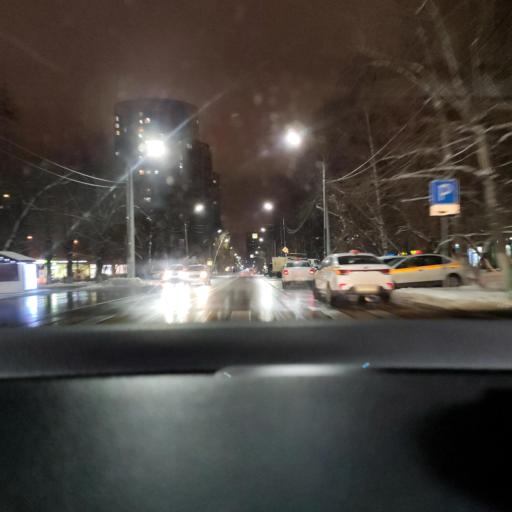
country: RU
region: Moskovskaya
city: Reutov
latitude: 55.7532
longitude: 37.8591
